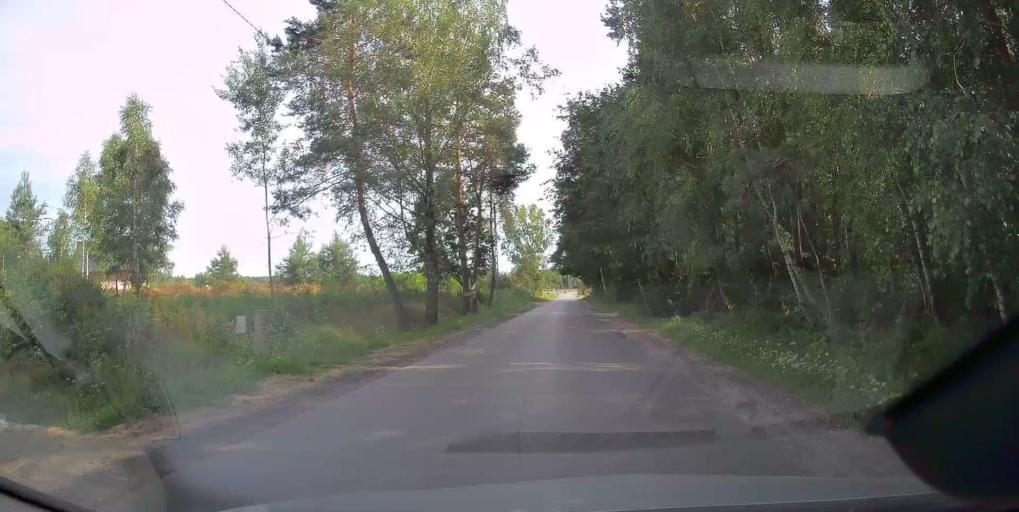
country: PL
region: Lodz Voivodeship
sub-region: Powiat tomaszowski
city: Tomaszow Mazowiecki
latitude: 51.4596
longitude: 20.0340
